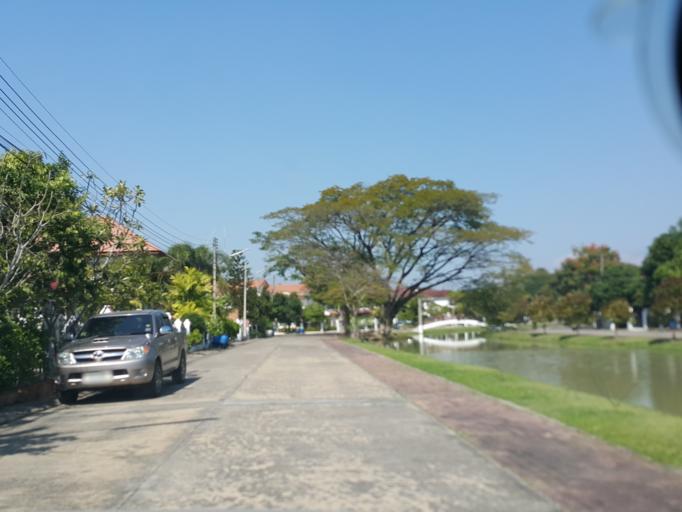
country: TH
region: Chiang Mai
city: Saraphi
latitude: 18.7568
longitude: 99.0248
